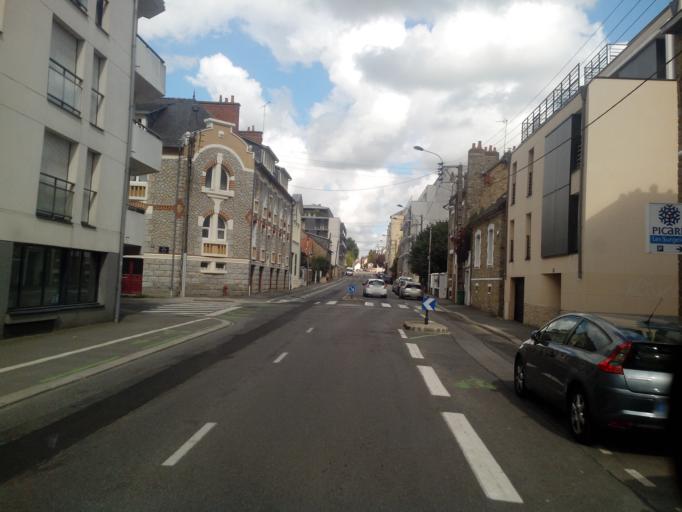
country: FR
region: Brittany
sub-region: Departement d'Ille-et-Vilaine
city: Rennes
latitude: 48.1191
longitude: -1.6606
